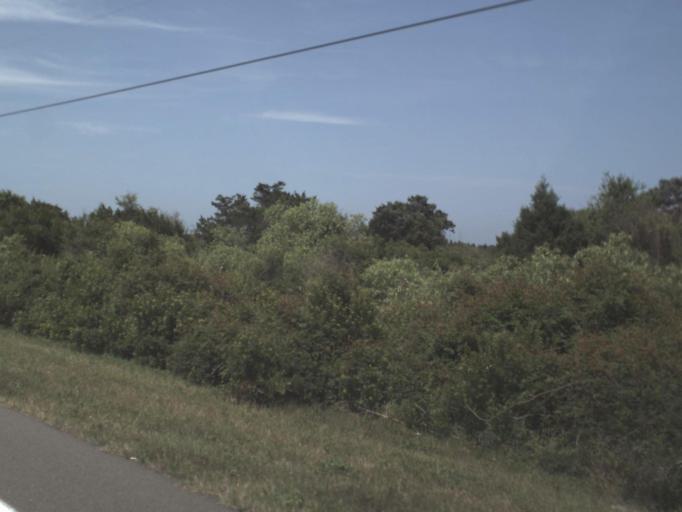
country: US
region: Florida
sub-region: Duval County
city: Atlantic Beach
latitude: 30.4517
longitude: -81.4156
